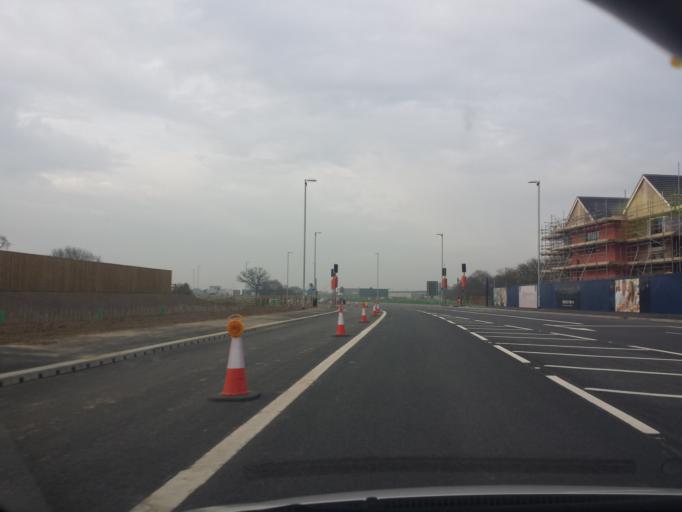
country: GB
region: England
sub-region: Essex
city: Colchester
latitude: 51.9197
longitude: 0.9033
